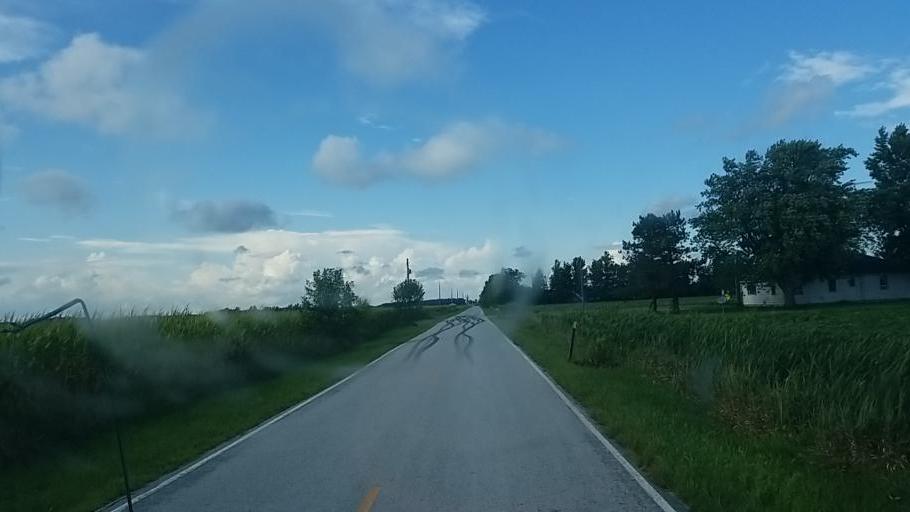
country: US
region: Ohio
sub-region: Hardin County
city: Forest
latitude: 40.7533
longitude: -83.4966
